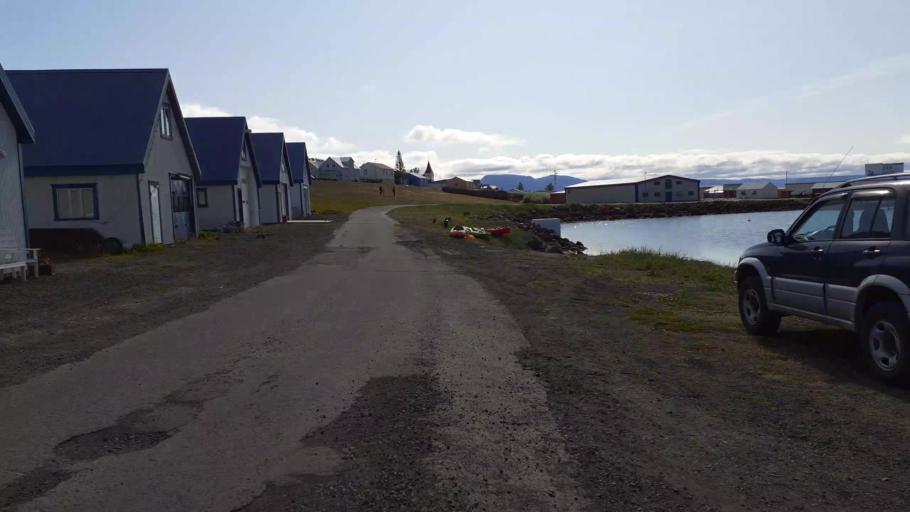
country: IS
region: Northeast
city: Dalvik
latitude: 65.9808
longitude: -18.3818
